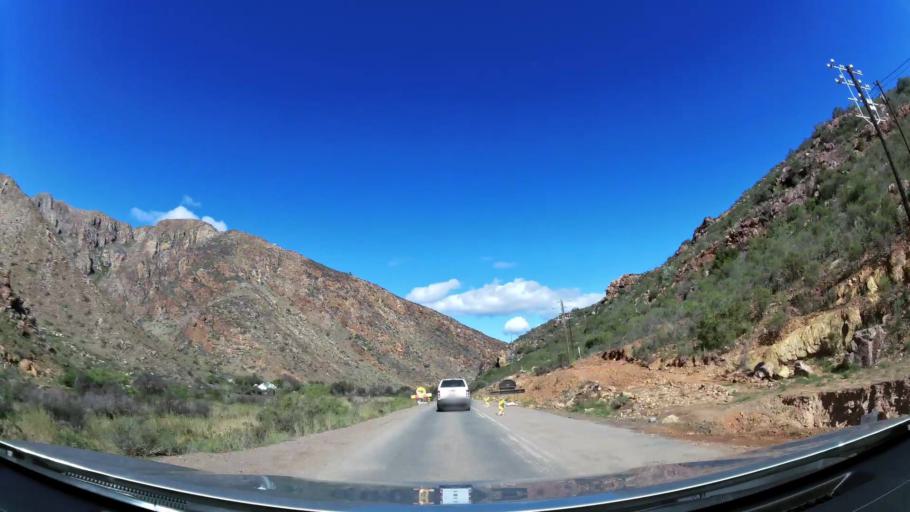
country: ZA
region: Western Cape
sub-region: Cape Winelands District Municipality
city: Ashton
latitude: -33.8085
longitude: 20.0940
